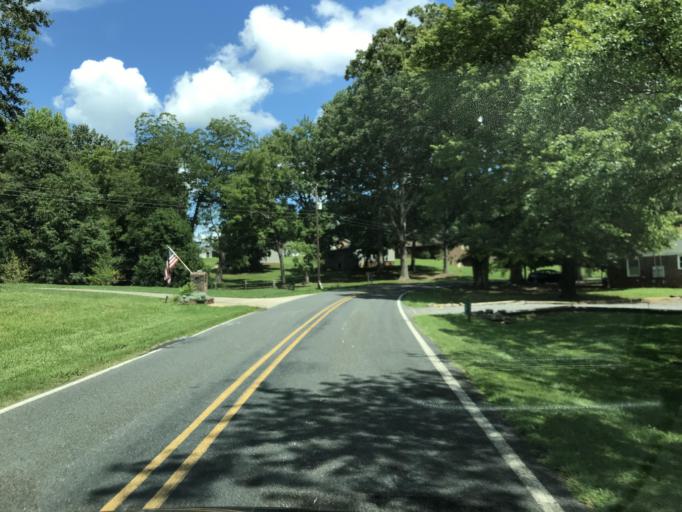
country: US
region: North Carolina
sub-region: Lincoln County
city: Pumpkin Center
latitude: 35.4996
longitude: -81.1909
